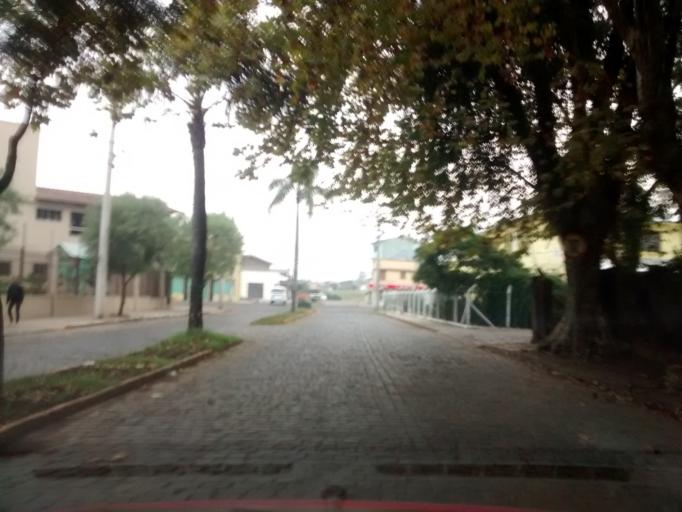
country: BR
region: Rio Grande do Sul
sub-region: Vacaria
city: Vacaria
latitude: -28.5032
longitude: -50.9329
